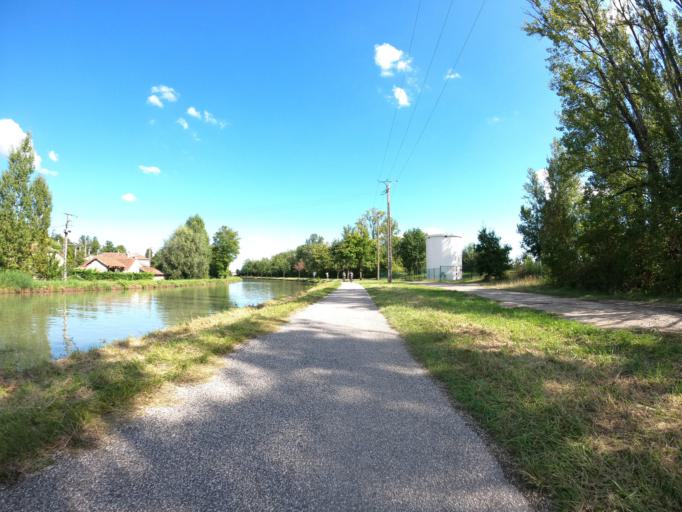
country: FR
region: Midi-Pyrenees
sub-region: Departement du Tarn-et-Garonne
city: Saint-Nicolas-de-la-Grave
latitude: 44.0835
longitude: 0.9804
